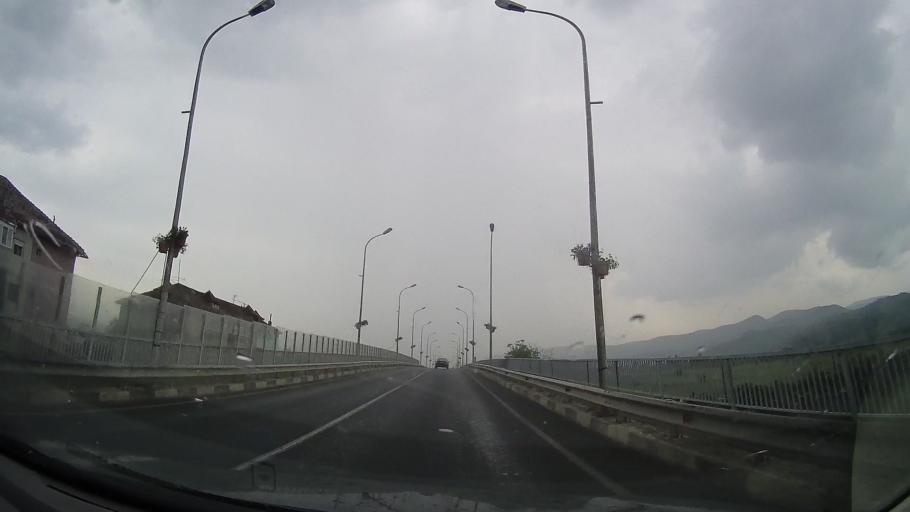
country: RO
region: Caras-Severin
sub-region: Comuna Buchin
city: Buchin
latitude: 45.3856
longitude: 22.2303
